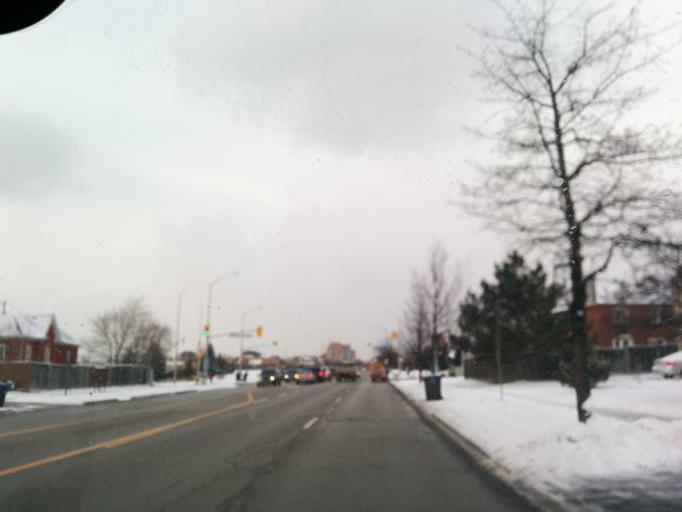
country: CA
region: Ontario
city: Mississauga
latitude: 43.5675
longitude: -79.7307
